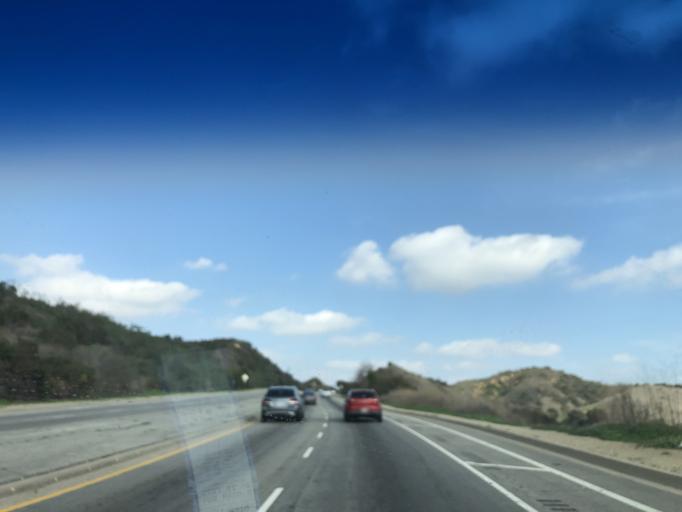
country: US
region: California
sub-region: Los Angeles County
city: Hacienda Heights
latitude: 33.9701
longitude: -117.9917
